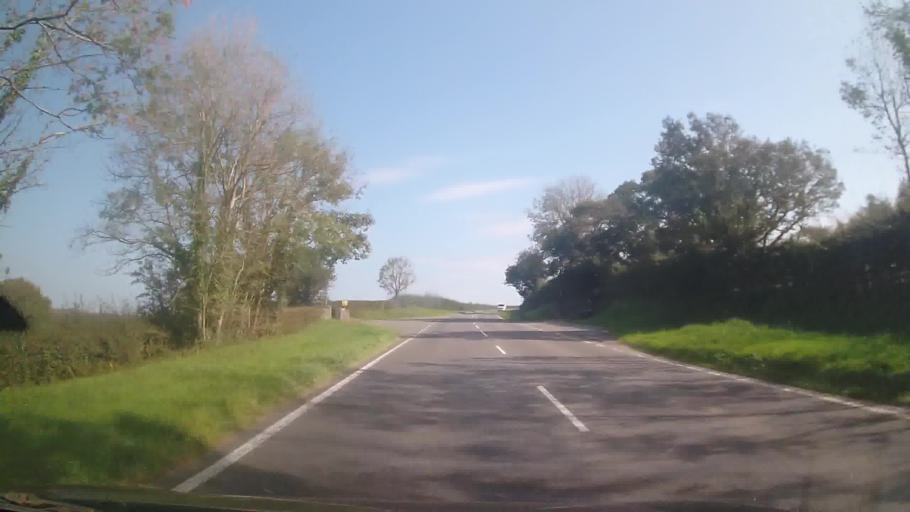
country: GB
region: Wales
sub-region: Pembrokeshire
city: Nevern
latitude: 52.0121
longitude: -4.7494
